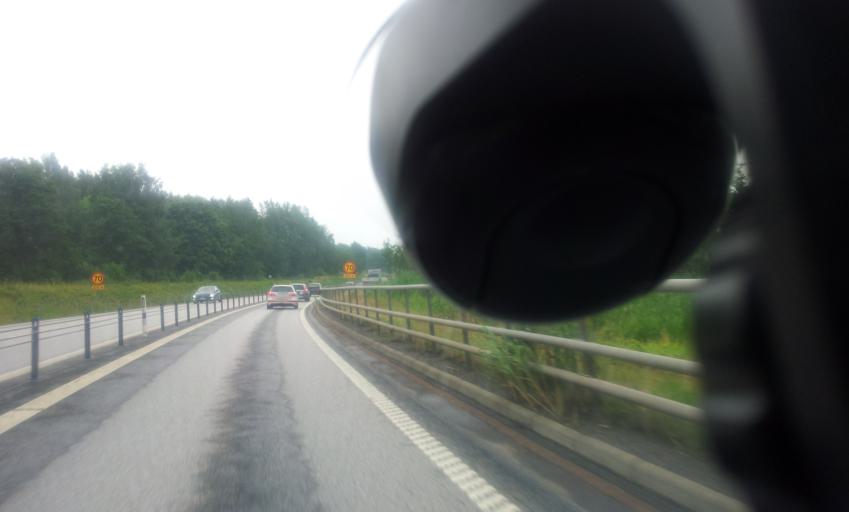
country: SE
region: Kalmar
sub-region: Vasterviks Kommun
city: Vaestervik
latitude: 57.8035
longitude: 16.5074
